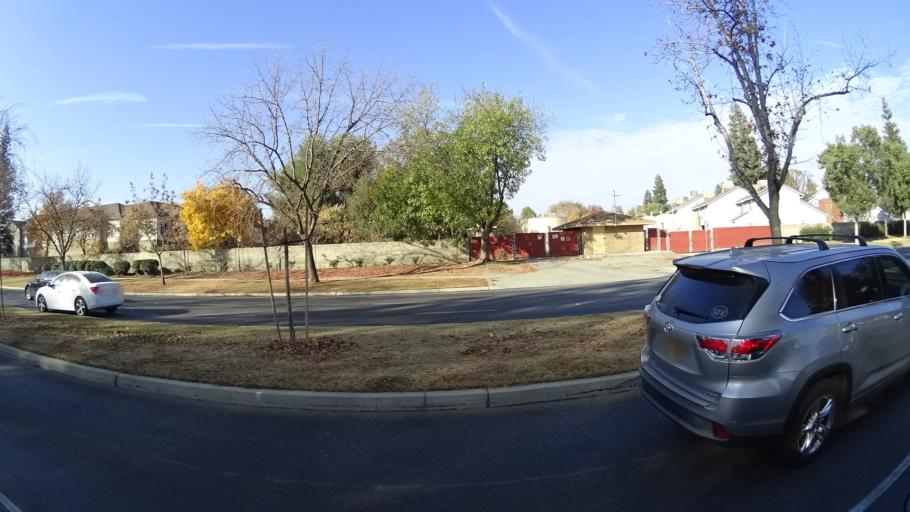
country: US
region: California
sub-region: Kern County
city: Greenacres
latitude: 35.3313
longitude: -119.0921
